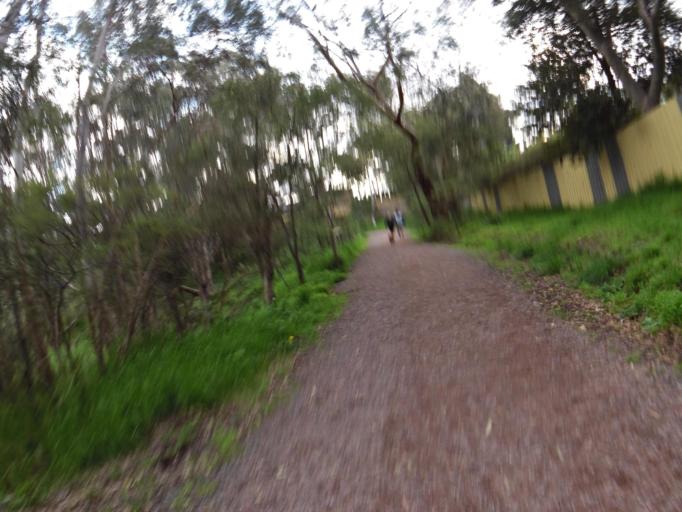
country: AU
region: Victoria
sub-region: Maroondah
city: Heathmont
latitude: -37.8386
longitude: 145.2381
